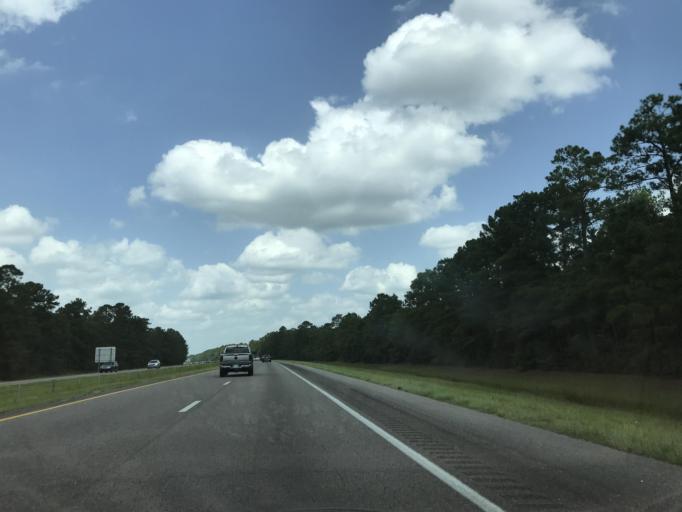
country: US
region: North Carolina
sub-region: Pender County
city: Burgaw
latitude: 34.5842
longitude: -77.9046
